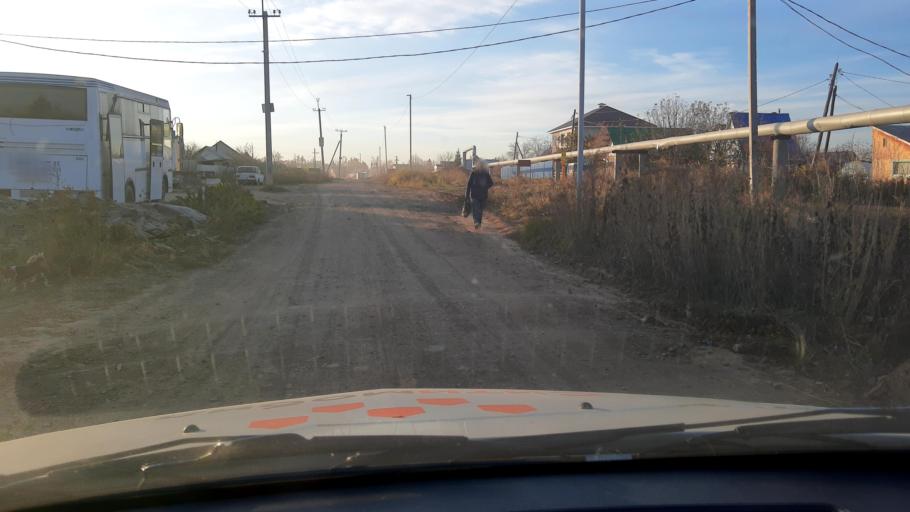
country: RU
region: Bashkortostan
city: Ufa
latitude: 54.8155
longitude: 56.1545
